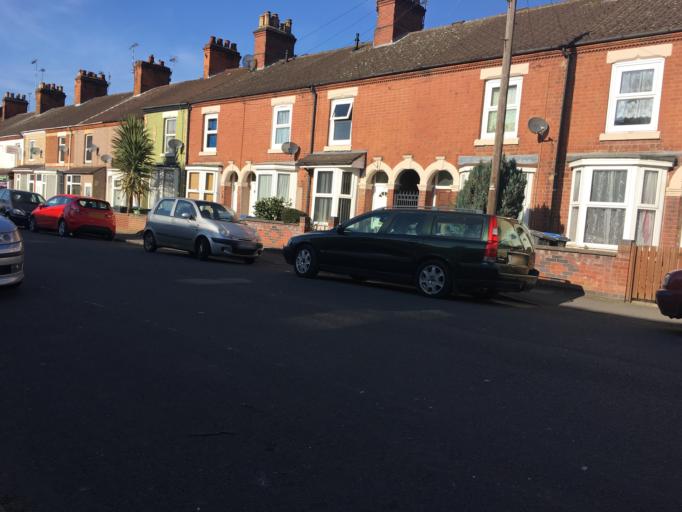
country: GB
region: England
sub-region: Warwickshire
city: Rugby
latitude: 52.3773
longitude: -1.2466
